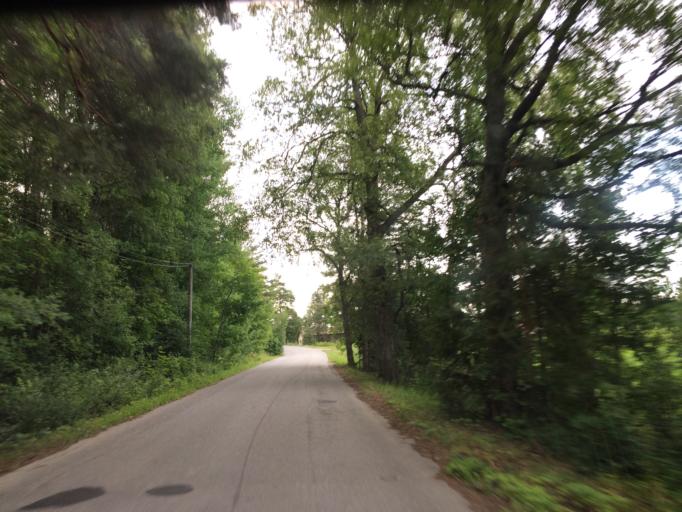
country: FI
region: Haeme
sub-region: Haemeenlinna
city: Tervakoski
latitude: 60.8389
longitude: 24.6265
